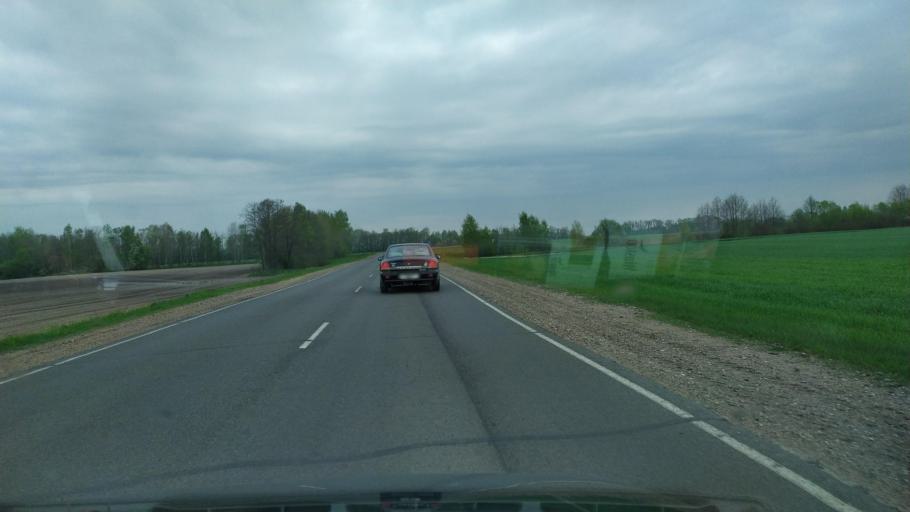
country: BY
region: Brest
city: Horad Kobryn
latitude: 52.2373
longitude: 24.4101
